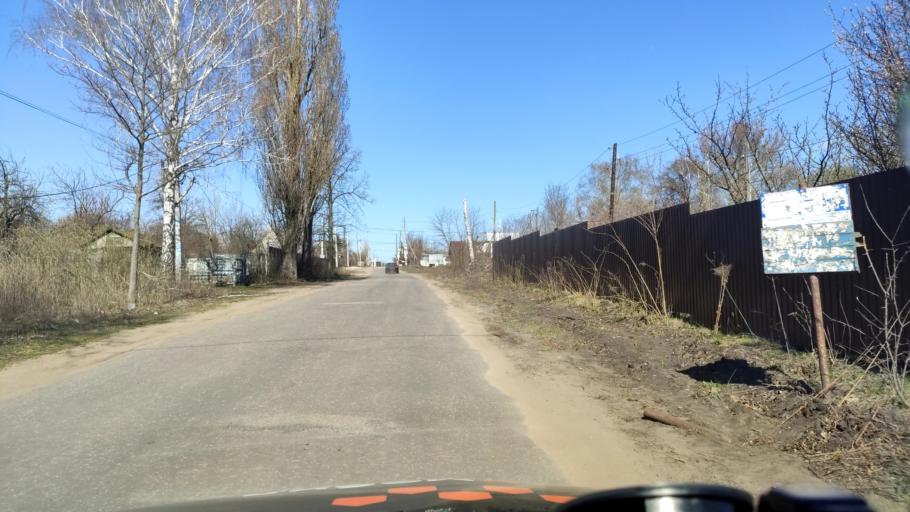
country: RU
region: Voronezj
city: Shilovo
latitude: 51.5973
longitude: 39.1489
